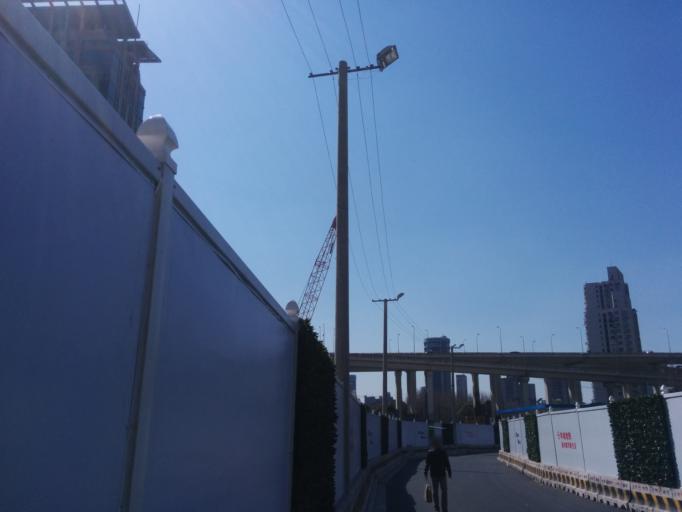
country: CN
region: Shanghai Shi
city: Shanghai
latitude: 31.2257
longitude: 121.4680
